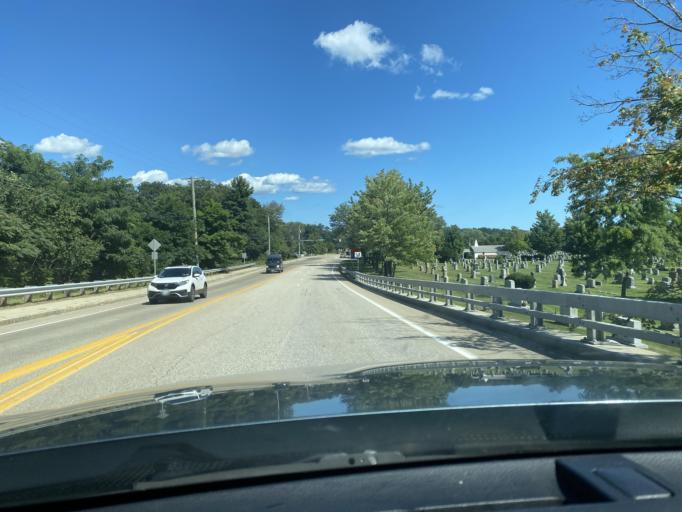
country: US
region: New Hampshire
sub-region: Rockingham County
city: Portsmouth
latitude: 43.0570
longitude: -70.7878
